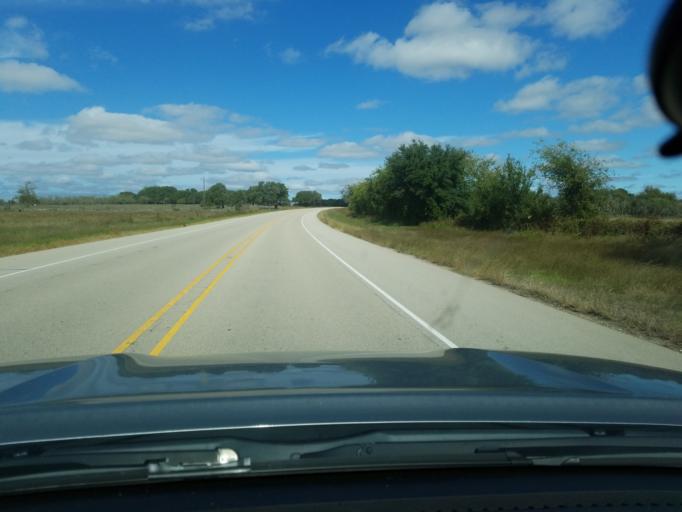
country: US
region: Texas
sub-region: Hamilton County
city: Hamilton
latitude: 31.6126
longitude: -98.1590
